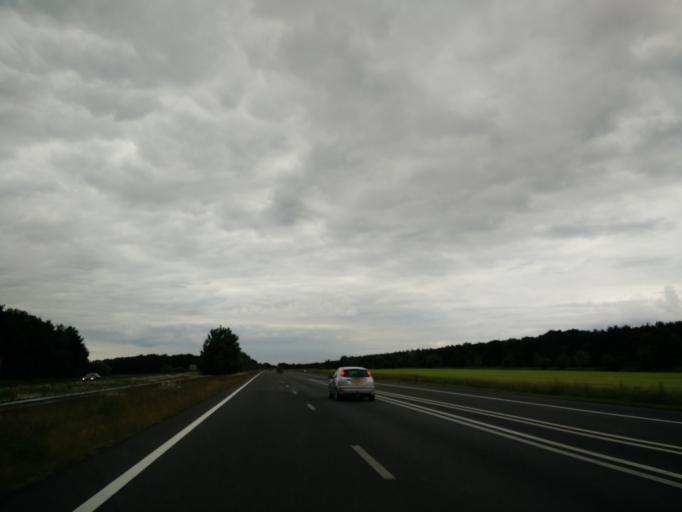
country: NL
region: Drenthe
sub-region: Gemeente Hoogeveen
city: Hoogeveen
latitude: 52.7428
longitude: 6.4633
